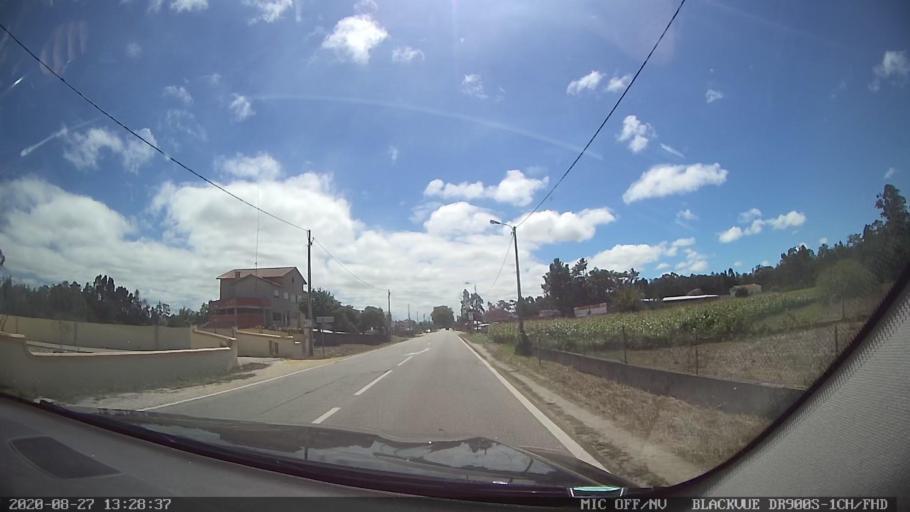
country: PT
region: Aveiro
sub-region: Vagos
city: Vagos
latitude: 40.5182
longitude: -8.6787
